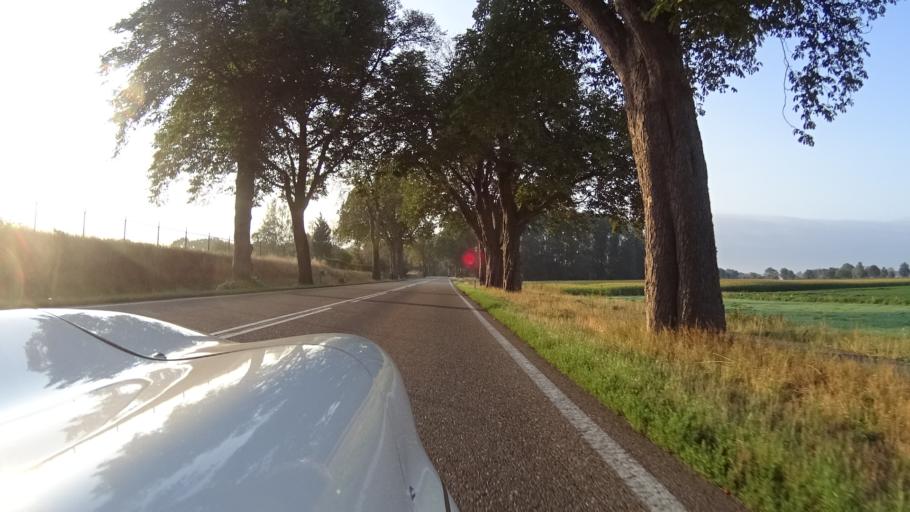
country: NL
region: Limburg
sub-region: Gemeente Bergen
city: Wellerlooi
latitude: 51.5511
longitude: 6.1107
